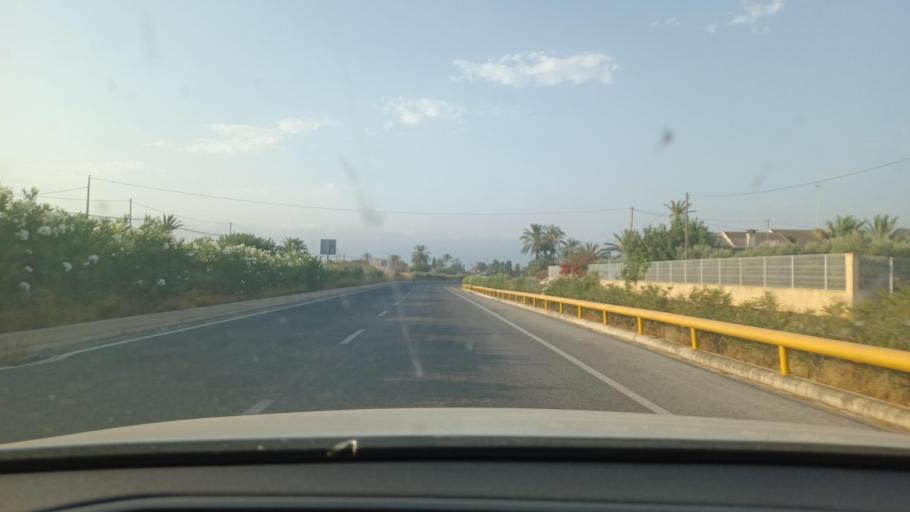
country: ES
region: Valencia
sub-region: Provincia de Alicante
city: Elche
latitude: 38.2204
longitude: -0.6975
